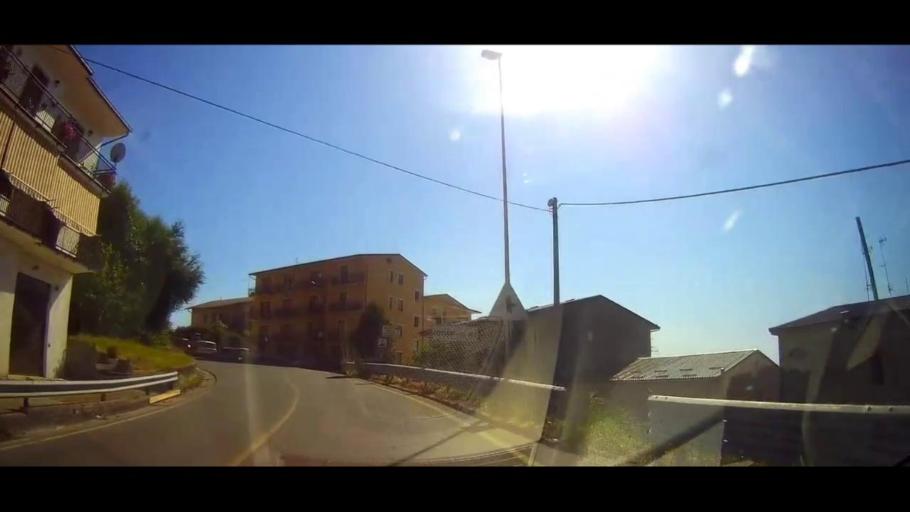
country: IT
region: Calabria
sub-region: Provincia di Cosenza
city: Celico
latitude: 39.3090
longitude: 16.3419
